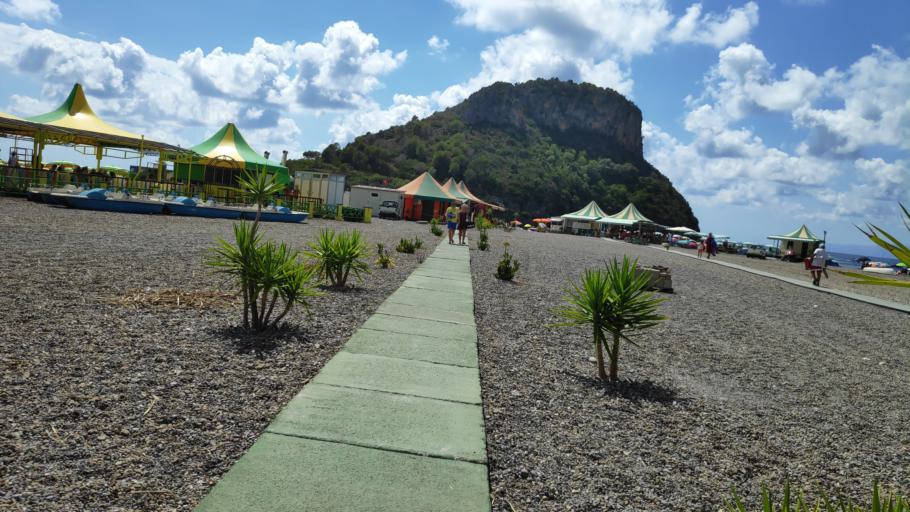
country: IT
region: Calabria
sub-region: Provincia di Cosenza
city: Praia a Mare
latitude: 39.8739
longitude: 15.7842
